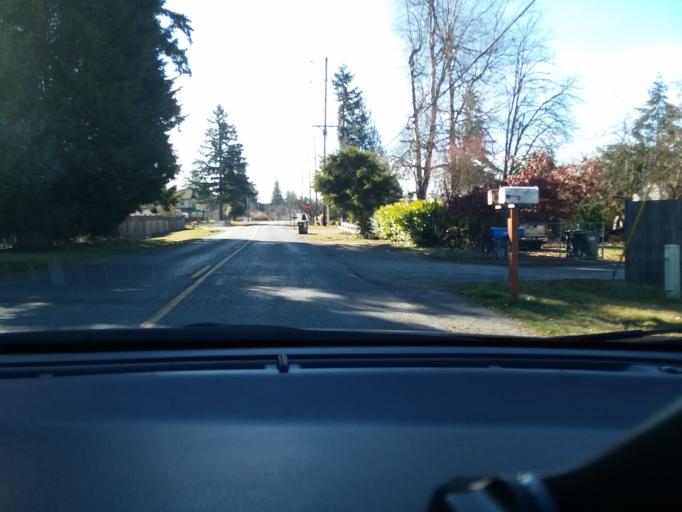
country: US
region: Washington
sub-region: Pierce County
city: Midland
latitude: 47.1707
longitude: -122.3972
